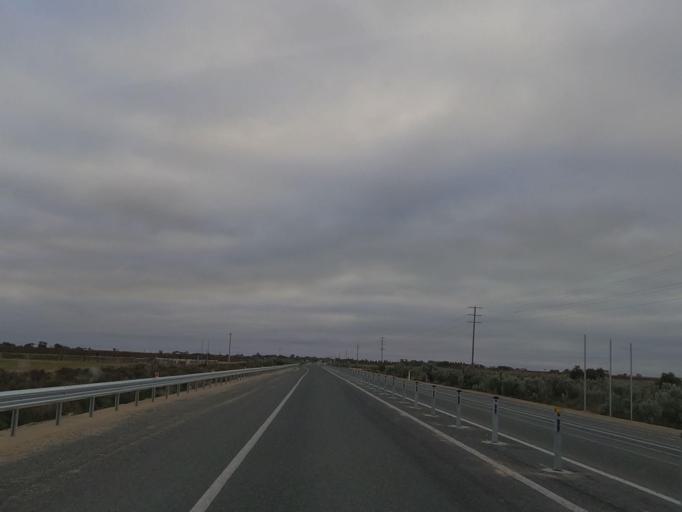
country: AU
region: Victoria
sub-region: Swan Hill
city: Swan Hill
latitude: -35.4749
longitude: 143.6772
